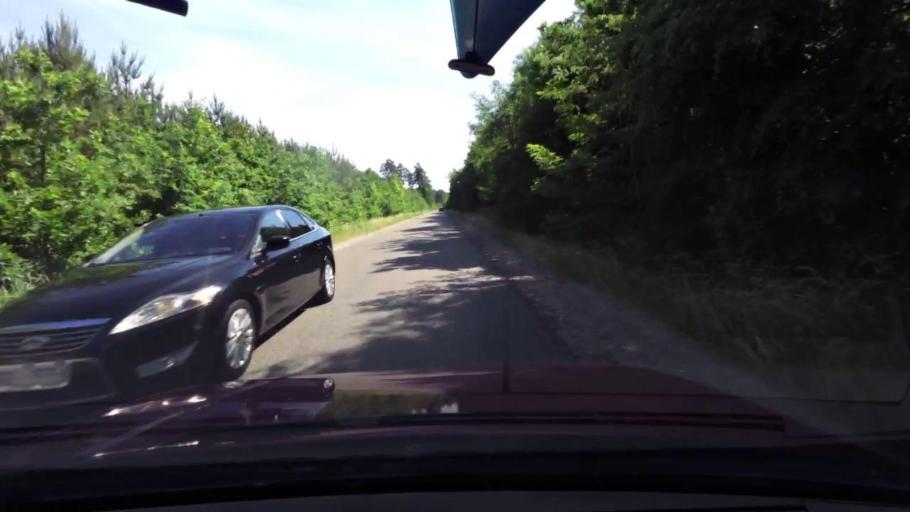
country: PL
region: Pomeranian Voivodeship
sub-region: Powiat slupski
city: Kepice
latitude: 54.3257
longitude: 16.9620
